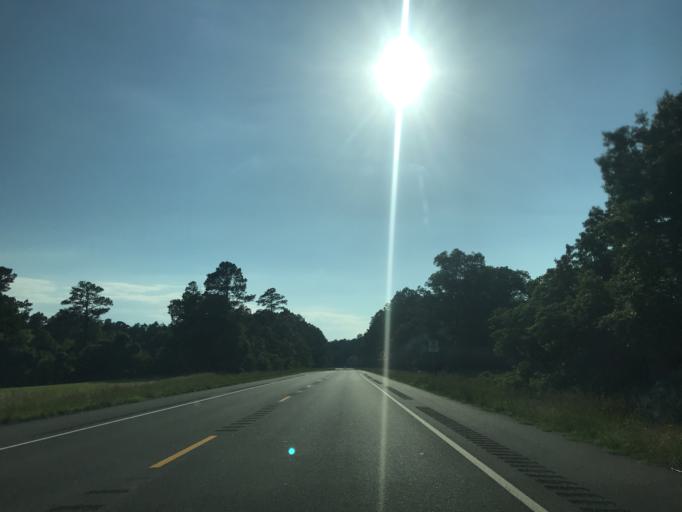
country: US
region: Maryland
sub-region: Wicomico County
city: Hebron
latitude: 38.5332
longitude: -75.7219
